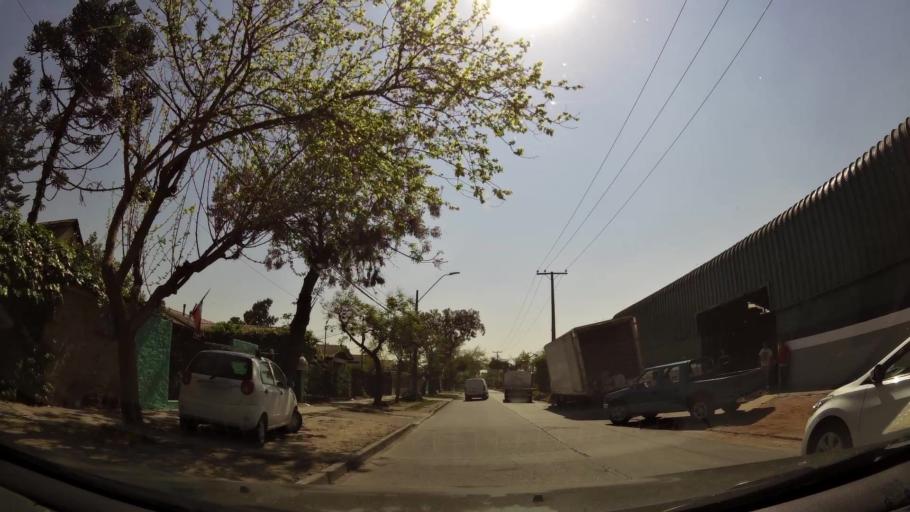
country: CL
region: Santiago Metropolitan
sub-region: Provincia de Maipo
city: San Bernardo
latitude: -33.6000
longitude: -70.7113
